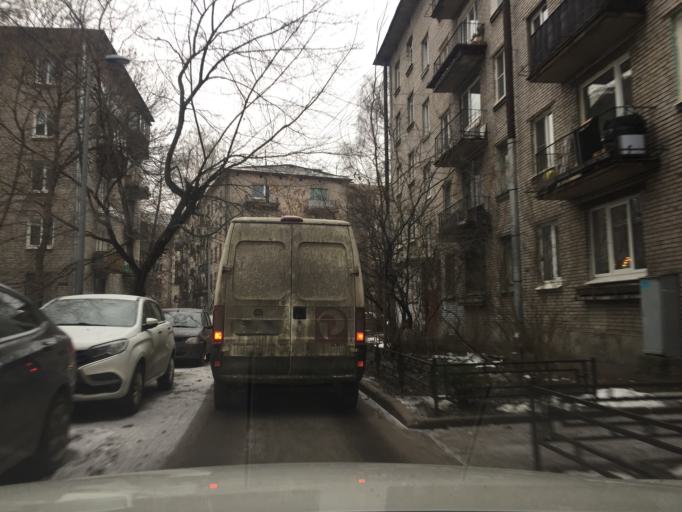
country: RU
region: St.-Petersburg
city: Vasyl'evsky Ostrov
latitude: 59.9419
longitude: 30.2346
